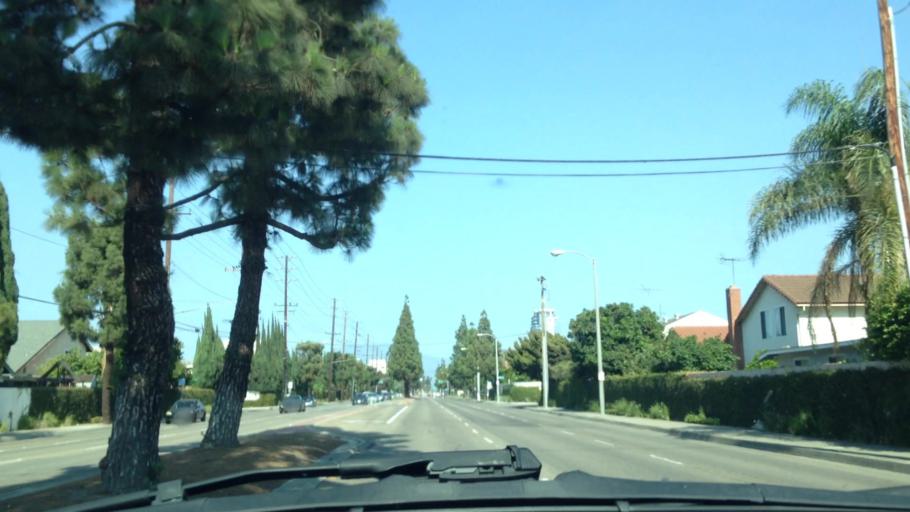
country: US
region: California
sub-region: Orange County
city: Santa Ana
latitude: 33.7000
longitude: -117.8757
